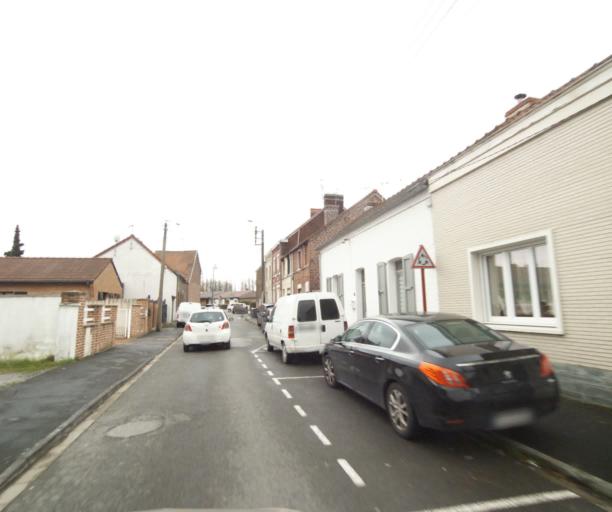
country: FR
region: Nord-Pas-de-Calais
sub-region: Departement du Nord
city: Petite-Foret
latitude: 50.3707
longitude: 3.4928
